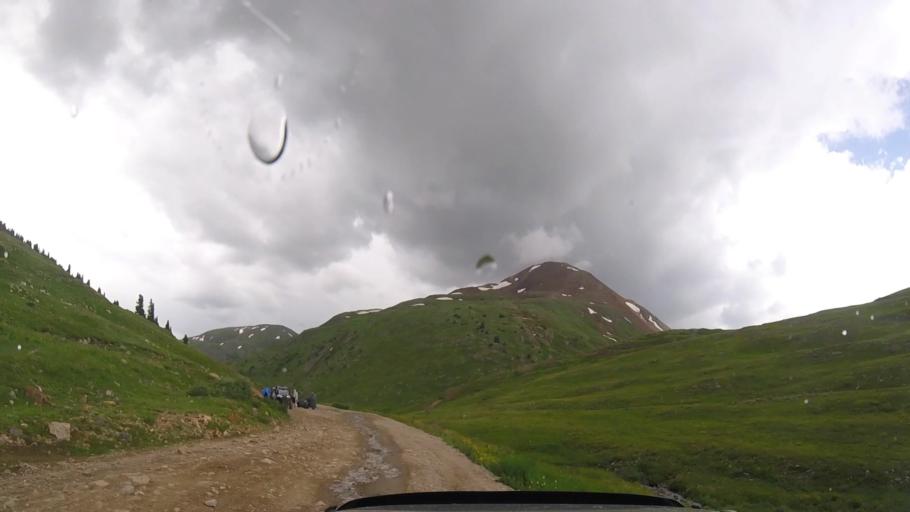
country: US
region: Colorado
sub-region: Ouray County
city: Ouray
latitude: 37.9489
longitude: -107.5734
